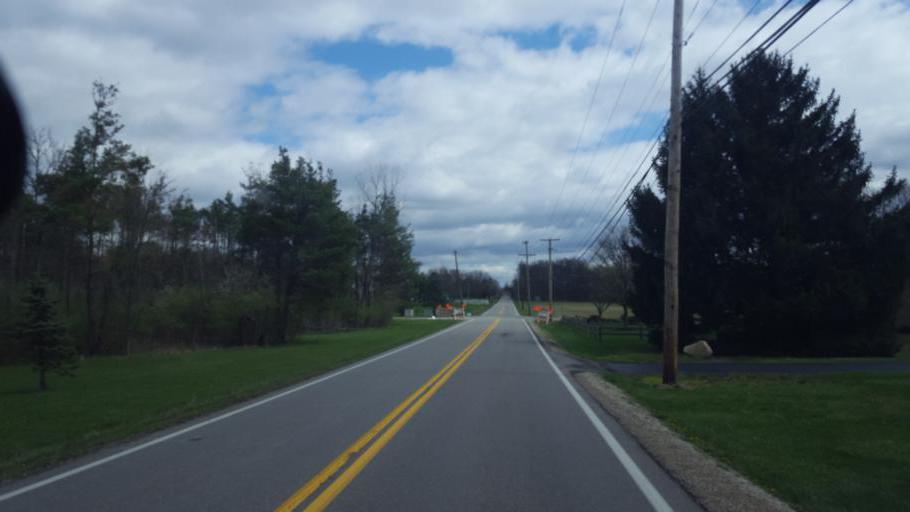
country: US
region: Ohio
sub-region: Franklin County
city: Westerville
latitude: 40.1300
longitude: -82.8595
